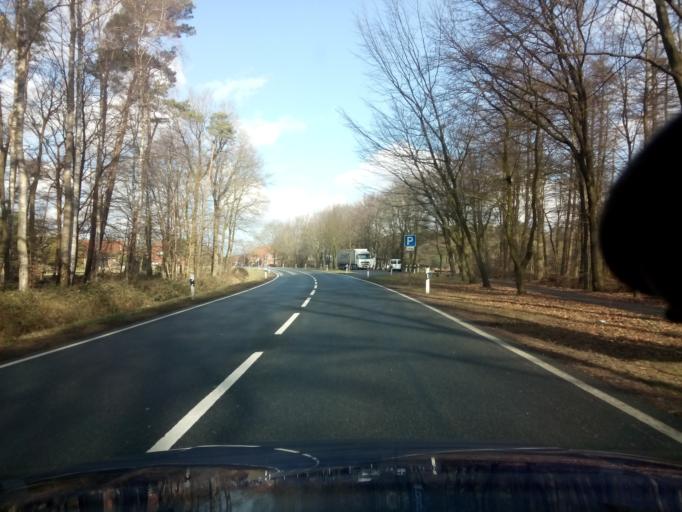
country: DE
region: Lower Saxony
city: Basdahl
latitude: 53.4251
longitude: 8.9930
